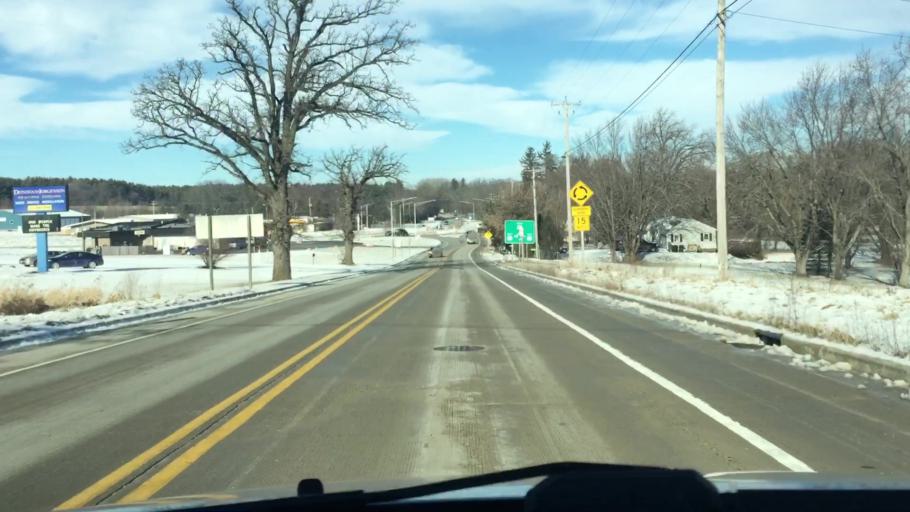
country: US
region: Wisconsin
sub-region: Waukesha County
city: North Prairie
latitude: 42.9557
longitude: -88.3589
